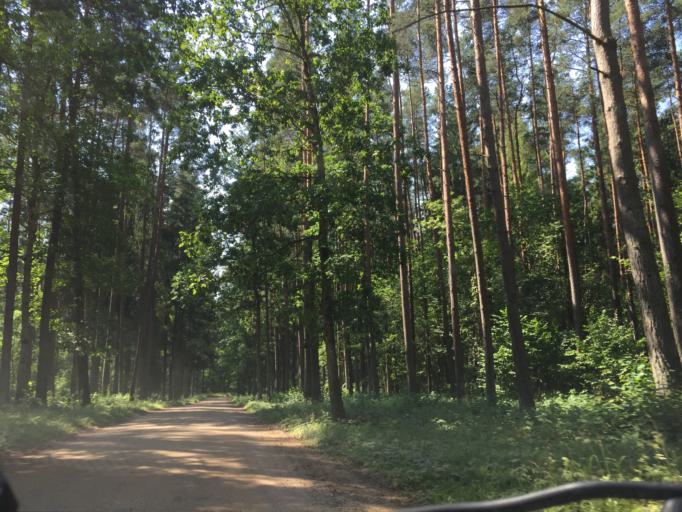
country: LV
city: Tervete
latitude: 56.4859
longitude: 23.4004
